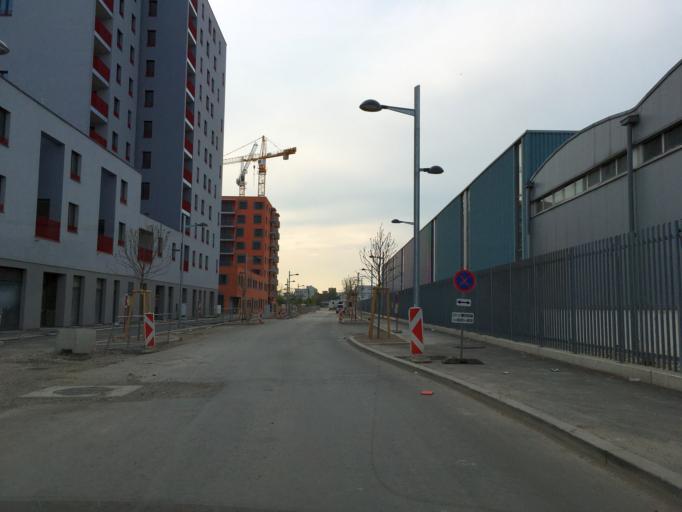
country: AT
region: Lower Austria
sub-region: Politischer Bezirk Wien-Umgebung
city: Gerasdorf bei Wien
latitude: 48.2642
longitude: 16.4223
